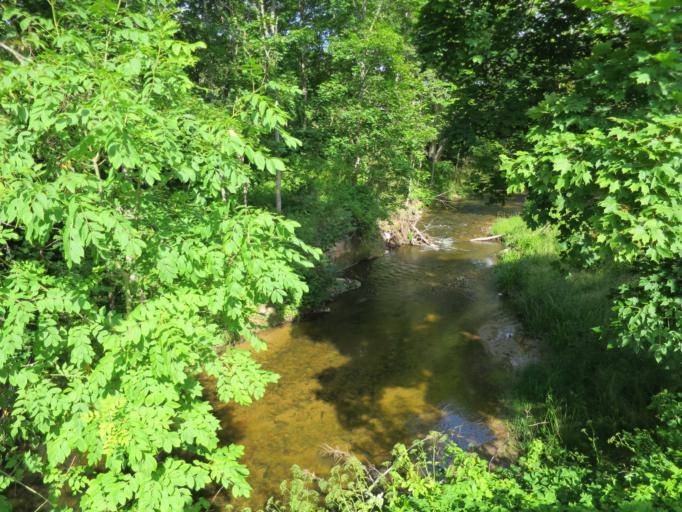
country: LV
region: Ligatne
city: Ligatne
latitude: 57.2316
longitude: 25.0444
